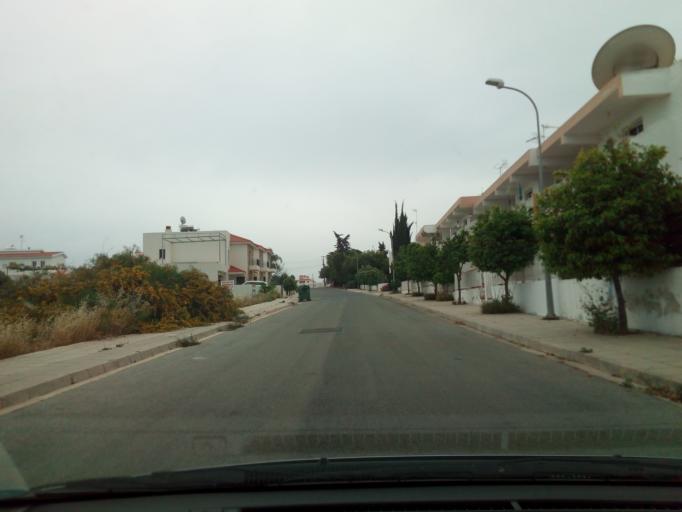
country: CY
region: Ammochostos
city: Paralimni
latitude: 35.0554
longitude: 33.9839
